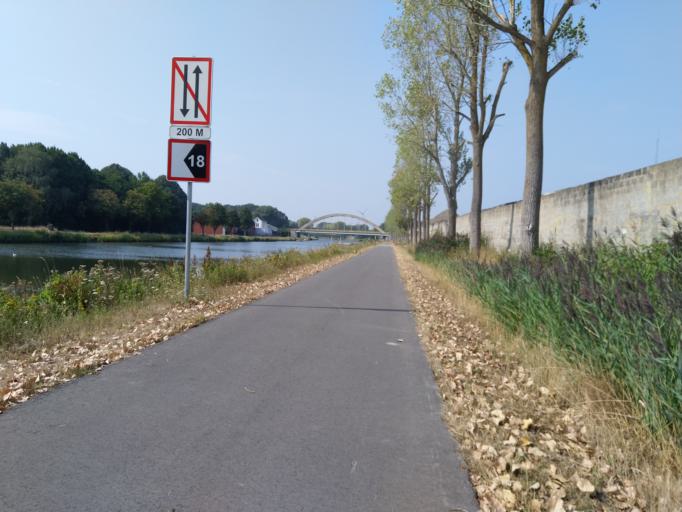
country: BE
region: Wallonia
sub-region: Province du Hainaut
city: Manage
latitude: 50.5144
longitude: 4.2172
